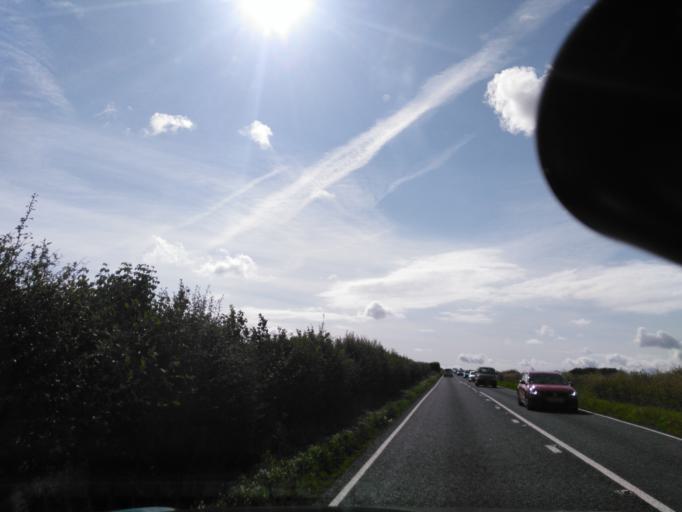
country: GB
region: England
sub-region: Wiltshire
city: Bishopstrow
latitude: 51.1515
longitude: -2.1670
